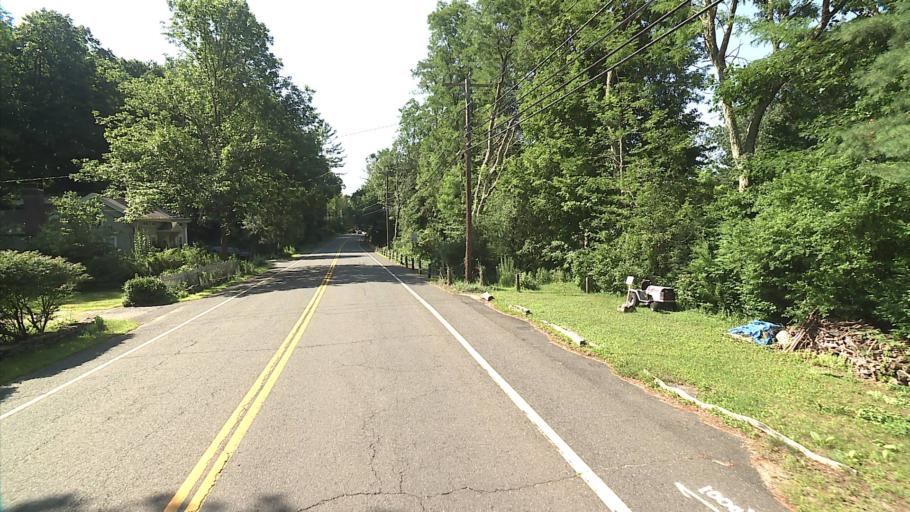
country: US
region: Connecticut
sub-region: Litchfield County
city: Winsted
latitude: 41.9655
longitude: -73.0175
